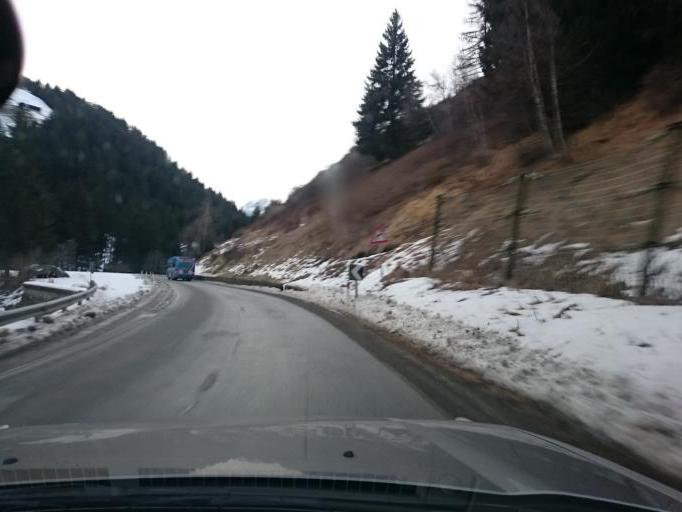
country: IT
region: Lombardy
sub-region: Provincia di Sondrio
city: Sant'Antonio
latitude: 46.4525
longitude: 10.4353
